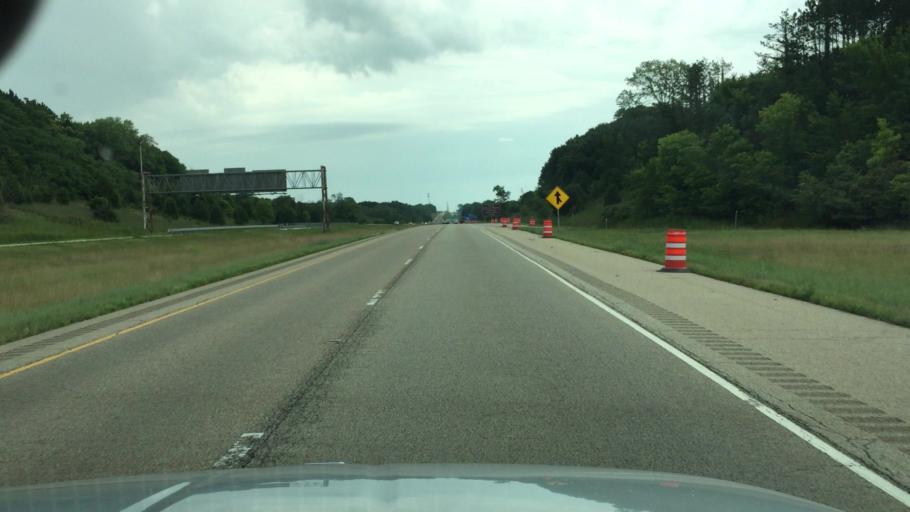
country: US
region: Illinois
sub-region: Peoria County
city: Bellevue
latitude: 40.7412
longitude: -89.6640
